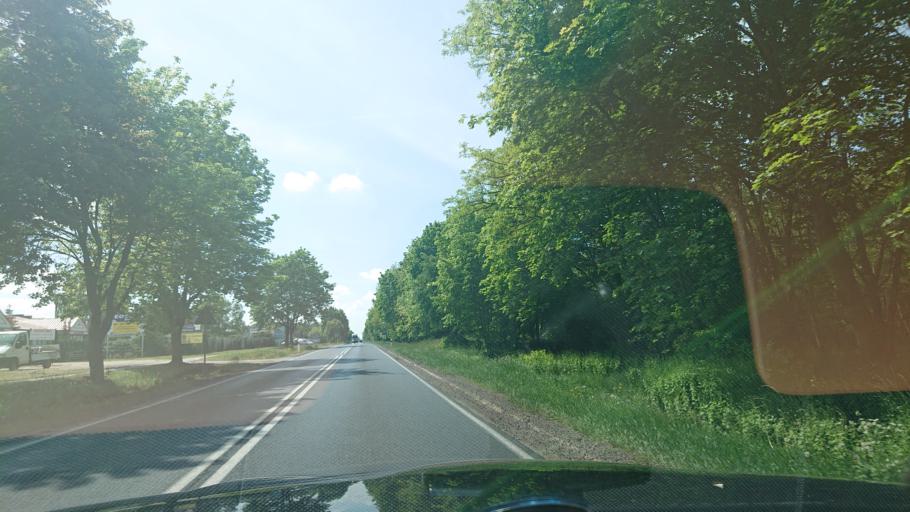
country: PL
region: Greater Poland Voivodeship
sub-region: Powiat gnieznienski
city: Gniezno
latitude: 52.4819
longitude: 17.5933
